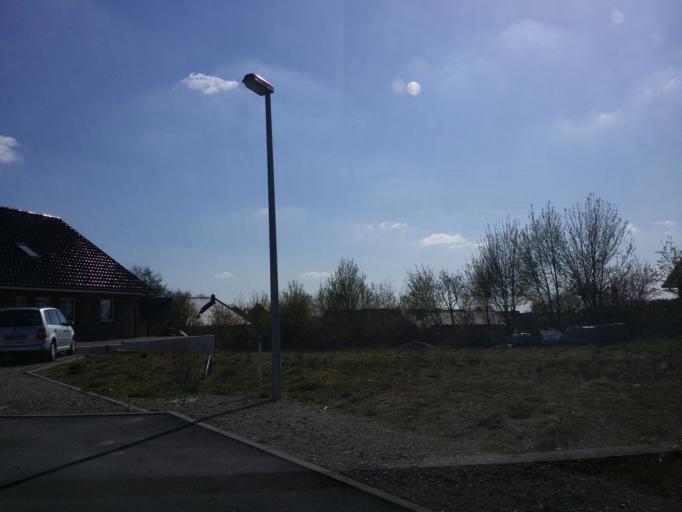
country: DE
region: Schleswig-Holstein
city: Wacken
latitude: 54.0249
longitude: 9.3835
